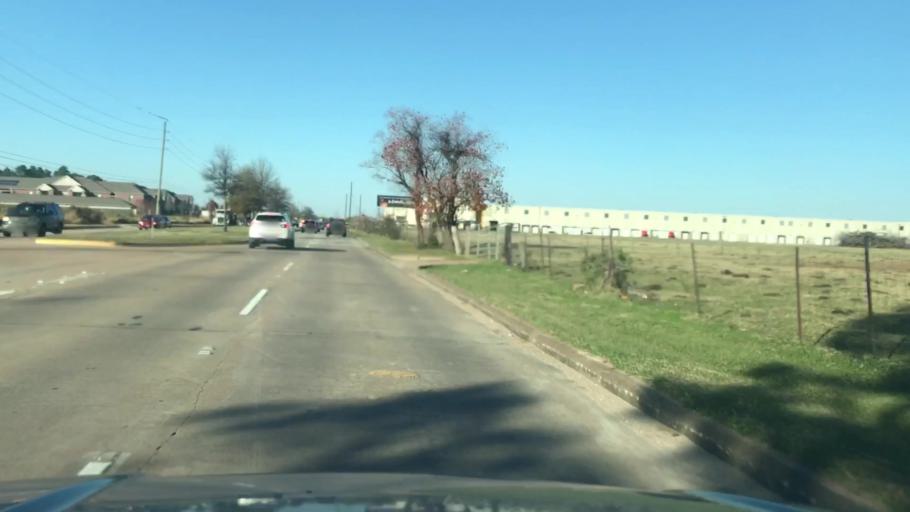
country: US
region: Texas
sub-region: Fort Bend County
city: Cinco Ranch
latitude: 29.8033
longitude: -95.7519
